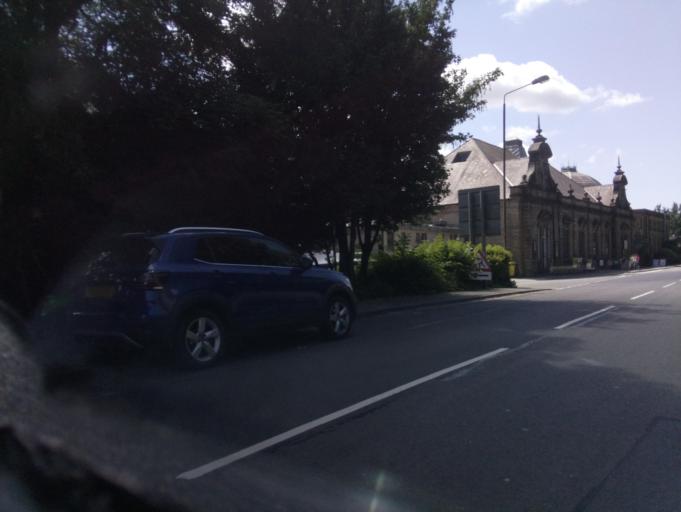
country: GB
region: England
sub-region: Derbyshire
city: Buxton
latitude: 53.2587
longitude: -1.9173
